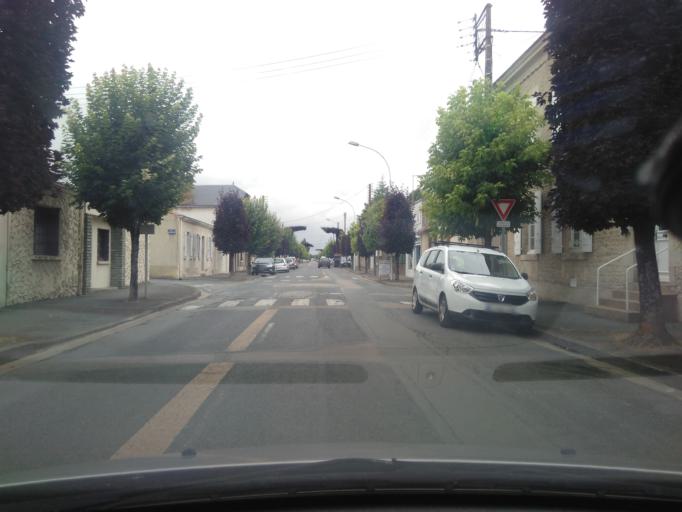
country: FR
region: Pays de la Loire
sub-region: Departement de la Vendee
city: Lucon
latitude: 46.4600
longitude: -1.1692
